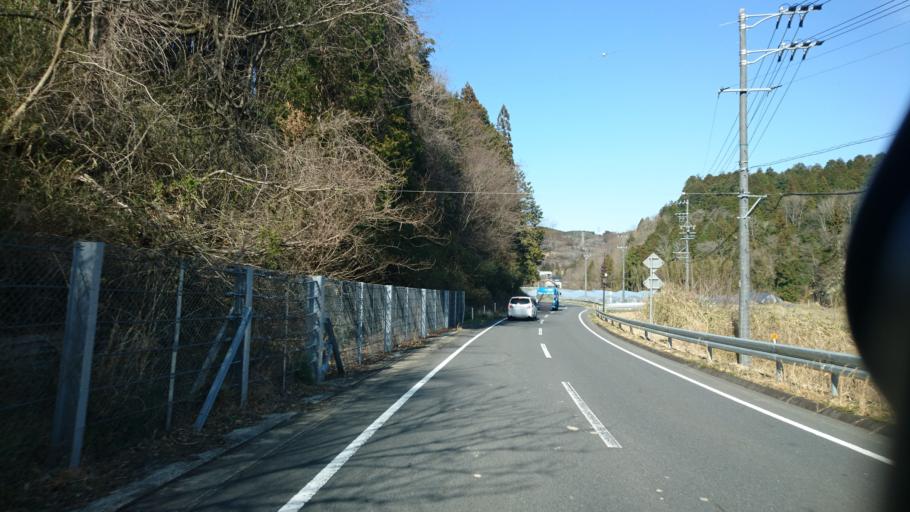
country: JP
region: Gifu
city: Nakatsugawa
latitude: 35.4593
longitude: 137.3737
